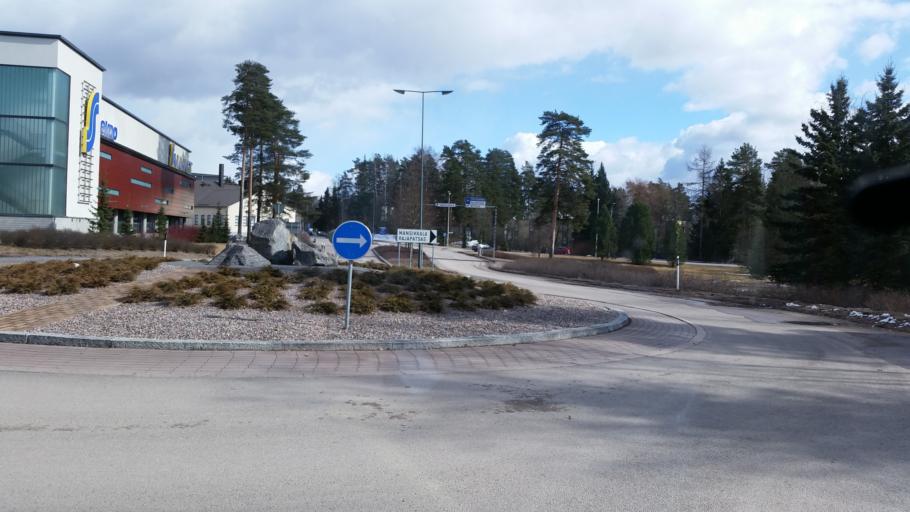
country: FI
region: South Karelia
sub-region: Imatra
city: Imatra
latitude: 61.1696
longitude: 28.7641
